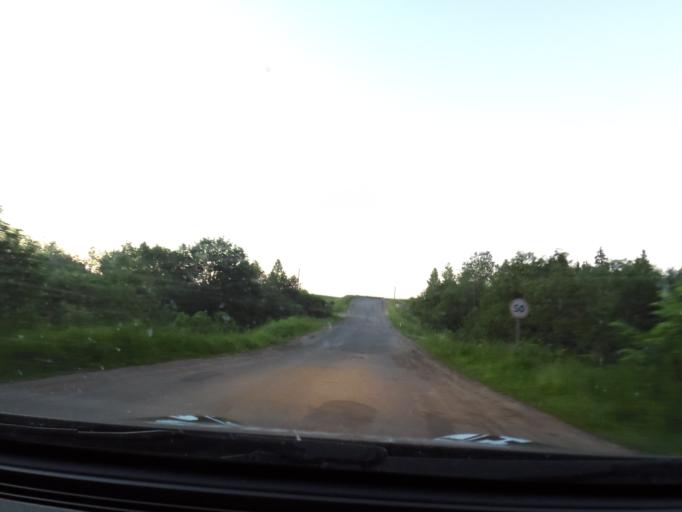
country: RU
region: Kostroma
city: Buy
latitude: 58.4788
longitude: 41.4405
